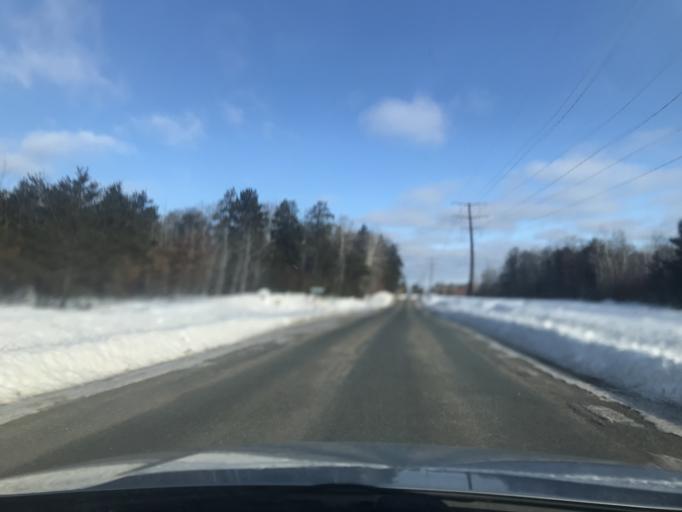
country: US
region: Wisconsin
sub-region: Marinette County
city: Niagara
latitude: 45.5942
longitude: -87.9769
